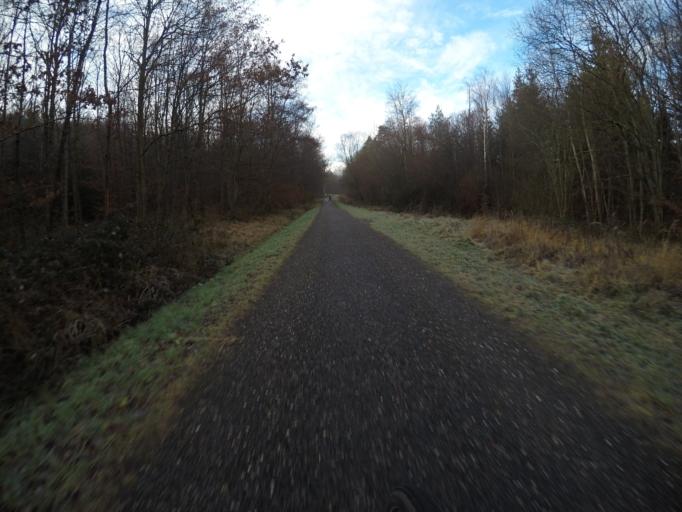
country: DE
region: Baden-Wuerttemberg
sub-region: Regierungsbezirk Stuttgart
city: Sindelfingen
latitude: 48.7226
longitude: 9.0257
